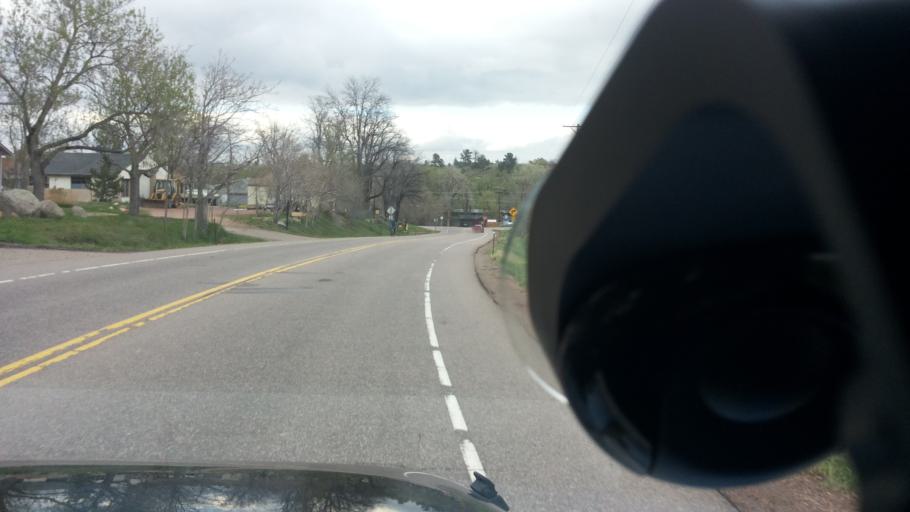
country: US
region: Colorado
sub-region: Boulder County
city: Superior
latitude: 39.9544
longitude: -105.2307
